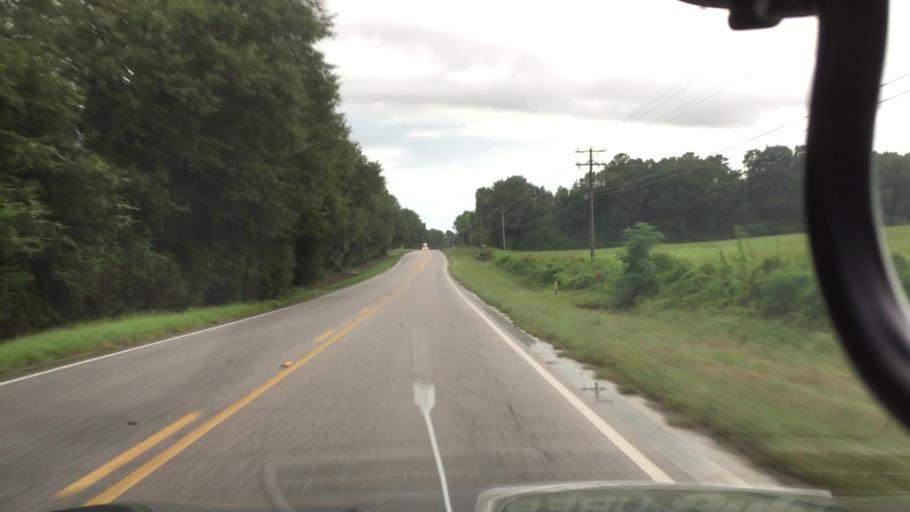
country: US
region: Alabama
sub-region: Pike County
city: Troy
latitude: 31.7339
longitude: -85.9575
